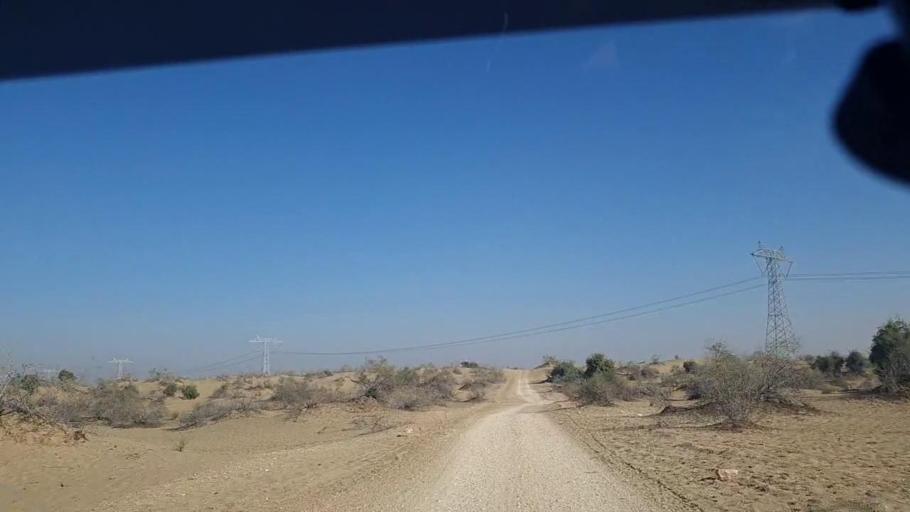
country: PK
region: Sindh
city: Khanpur
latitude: 27.6453
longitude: 69.4023
